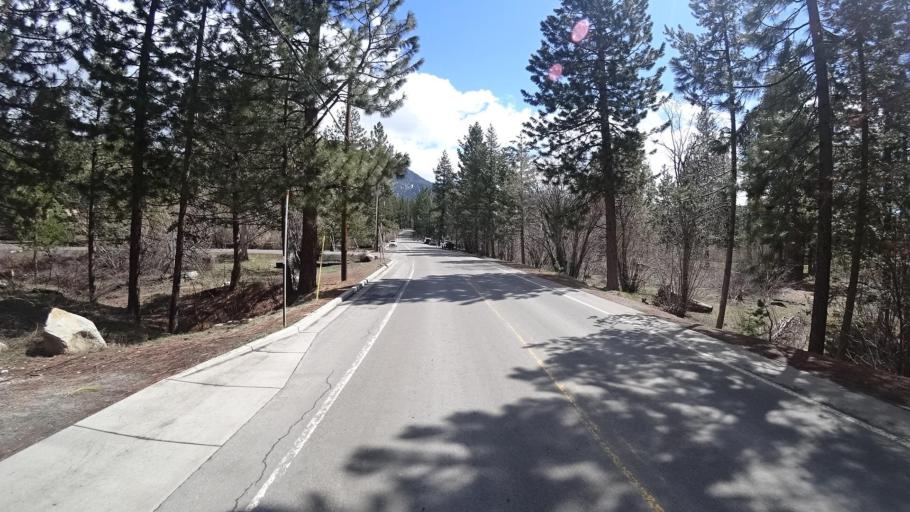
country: US
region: Nevada
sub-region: Washoe County
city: Incline Village
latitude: 39.2432
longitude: -119.9442
